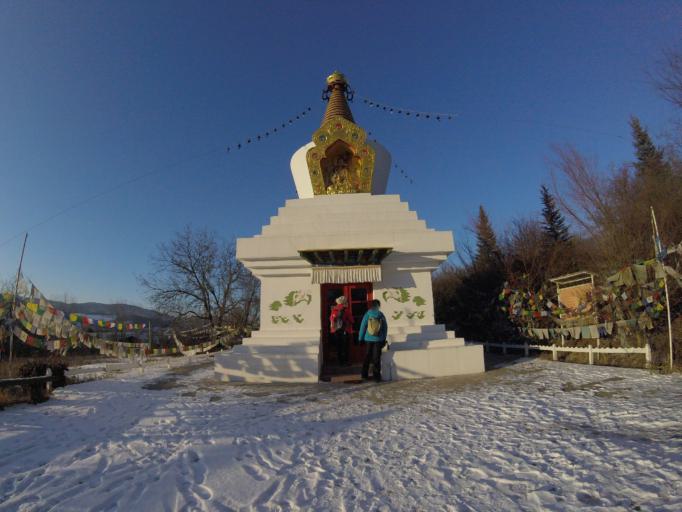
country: HU
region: Nograd
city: Tar
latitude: 47.9637
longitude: 19.7450
